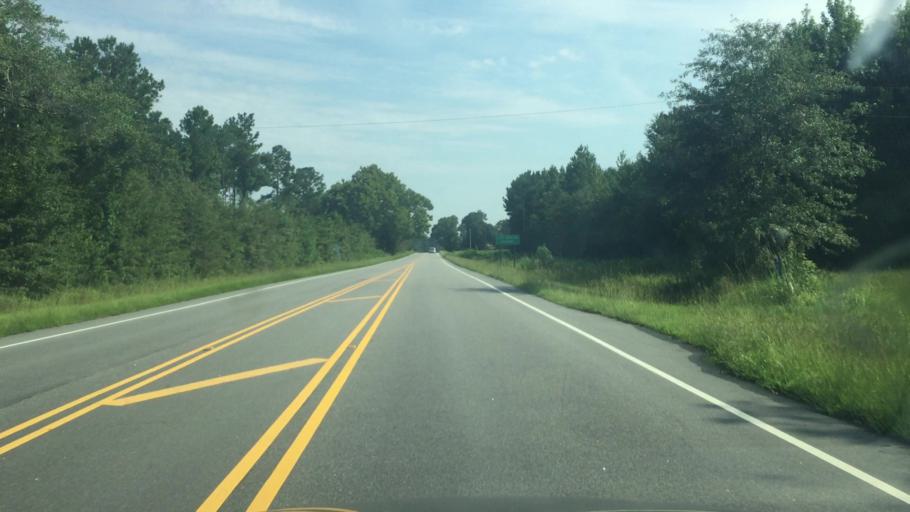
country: US
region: North Carolina
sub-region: Columbus County
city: Chadbourn
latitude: 34.2640
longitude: -78.8153
